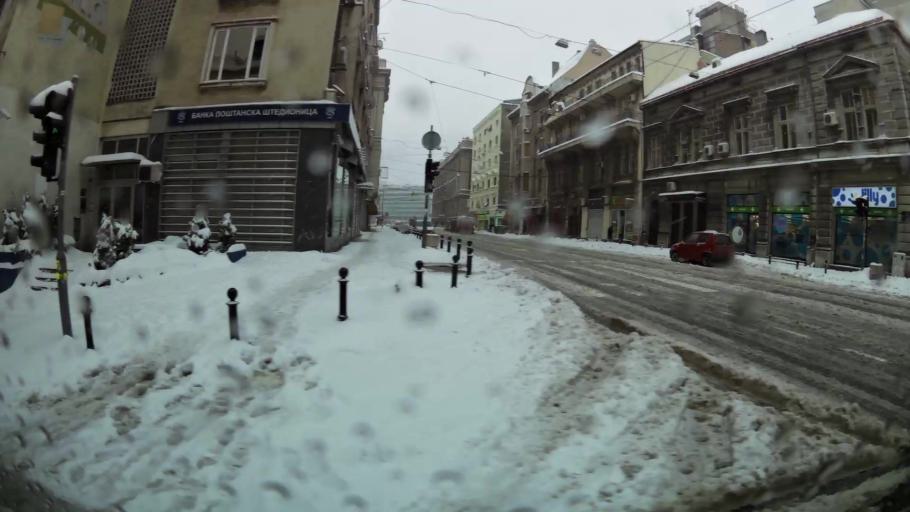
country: RS
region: Central Serbia
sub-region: Belgrade
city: Stari Grad
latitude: 44.8180
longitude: 20.4590
